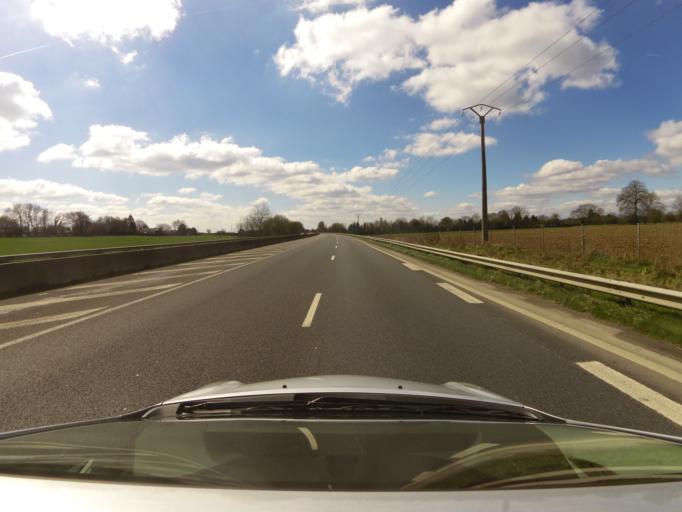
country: FR
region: Haute-Normandie
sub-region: Departement de la Seine-Maritime
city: Mesnieres-en-Bray
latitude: 49.6961
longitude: 1.3584
